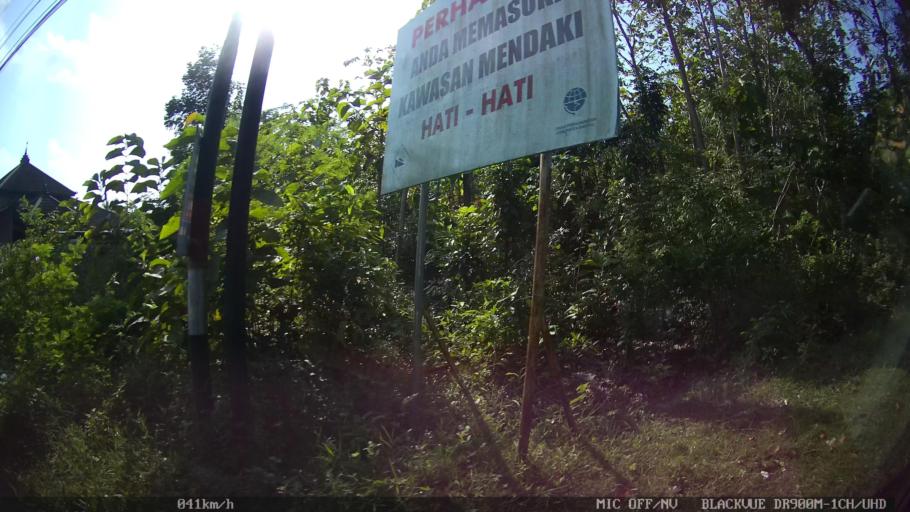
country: ID
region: Daerah Istimewa Yogyakarta
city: Godean
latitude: -7.8161
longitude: 110.2754
